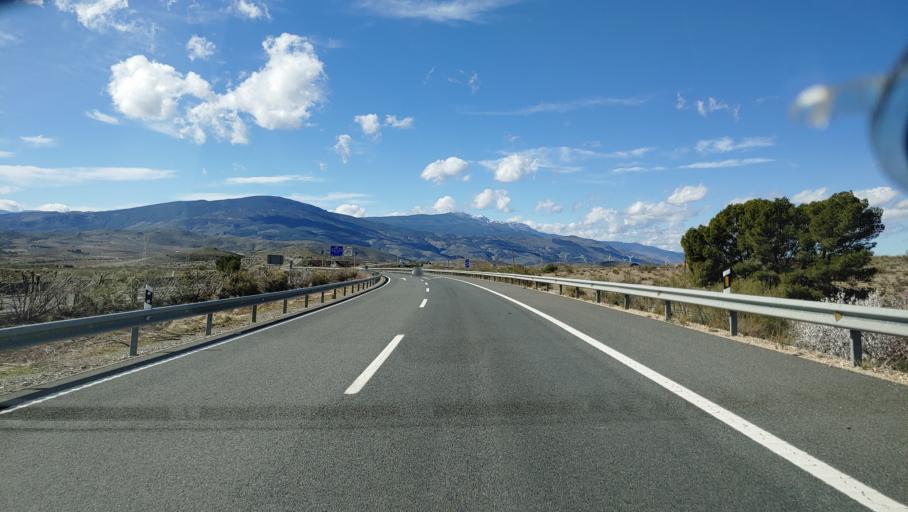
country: ES
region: Andalusia
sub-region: Provincia de Almeria
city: Gergal
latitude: 37.1197
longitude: -2.5835
